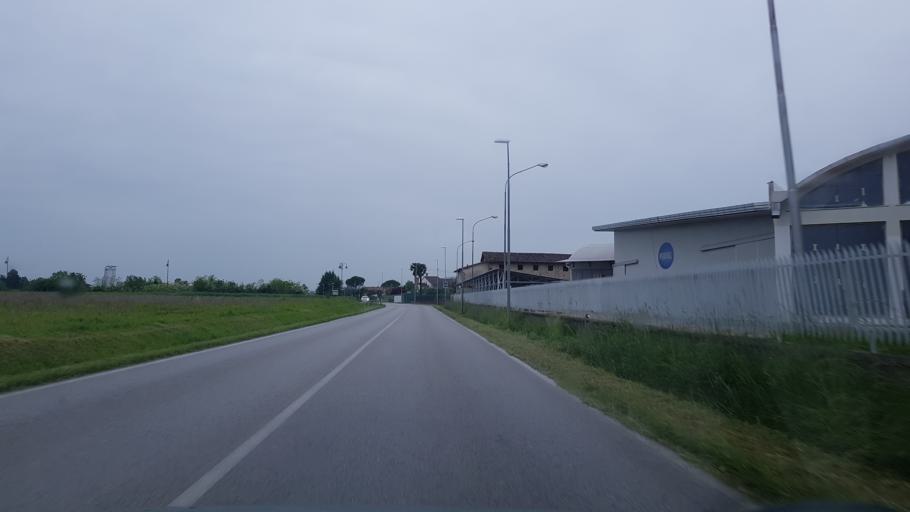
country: IT
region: Friuli Venezia Giulia
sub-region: Provincia di Udine
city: San Giovanni al Natisone
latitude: 45.9831
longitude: 13.4096
